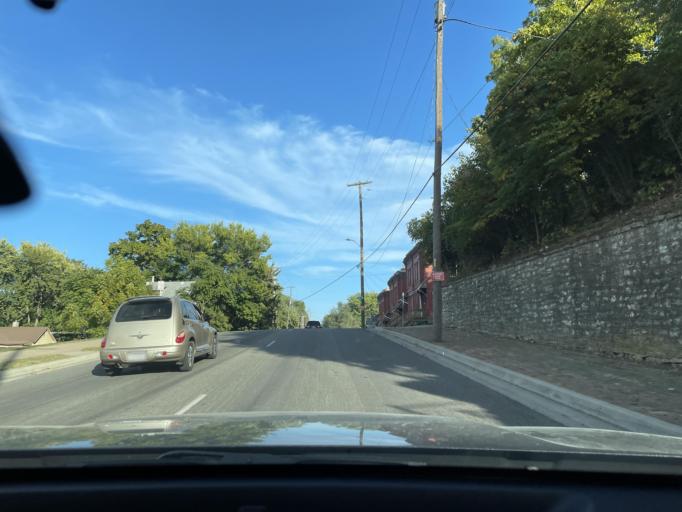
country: US
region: Missouri
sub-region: Buchanan County
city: Saint Joseph
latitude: 39.7683
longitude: -94.8430
